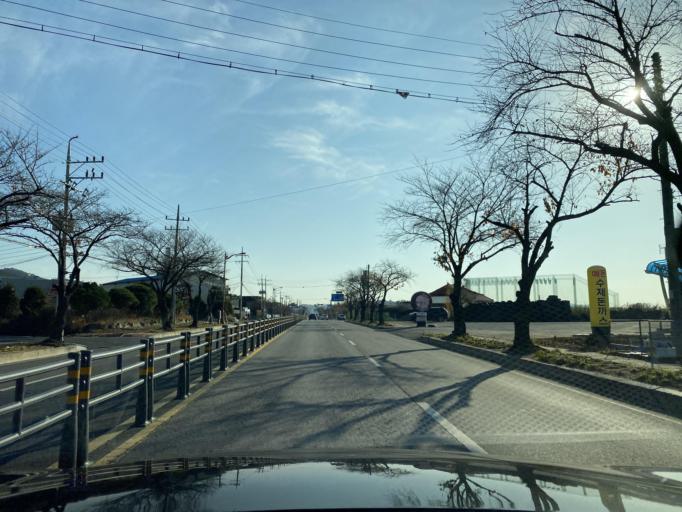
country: KR
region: Chungcheongnam-do
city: Yesan
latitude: 36.7099
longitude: 126.8402
